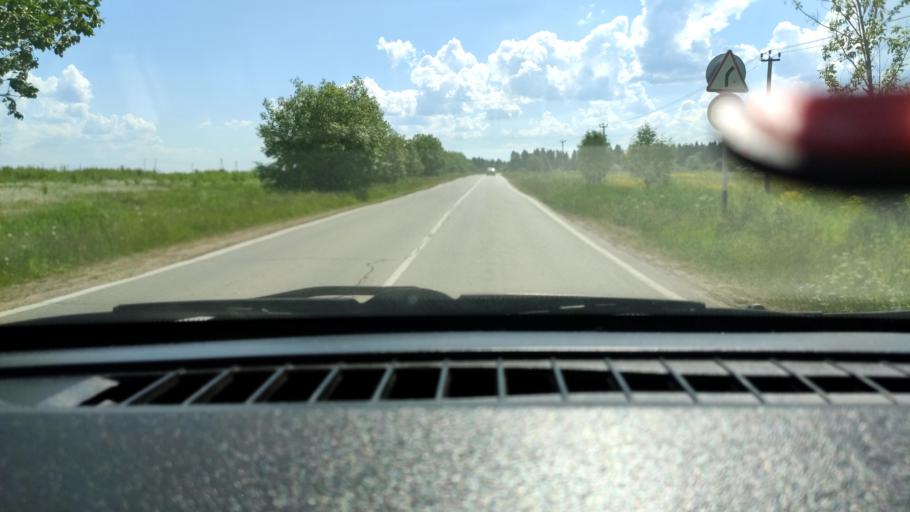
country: RU
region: Perm
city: Sylva
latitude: 58.0166
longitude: 56.7614
